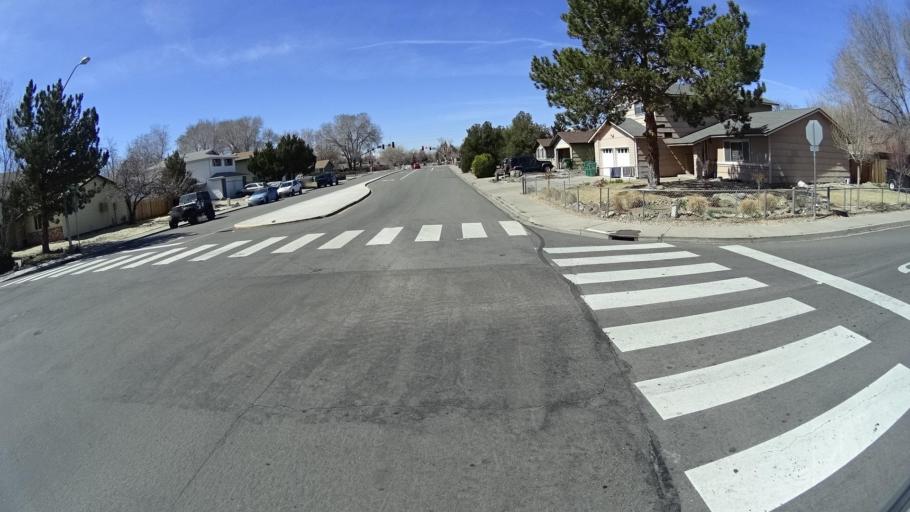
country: US
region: Nevada
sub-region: Washoe County
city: Sparks
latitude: 39.5472
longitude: -119.7322
